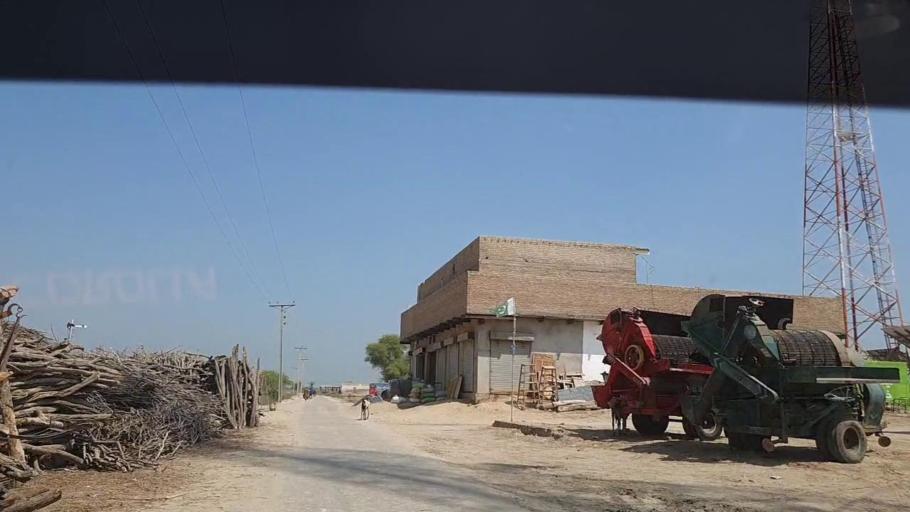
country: PK
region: Sindh
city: Tangwani
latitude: 28.2782
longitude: 69.0000
